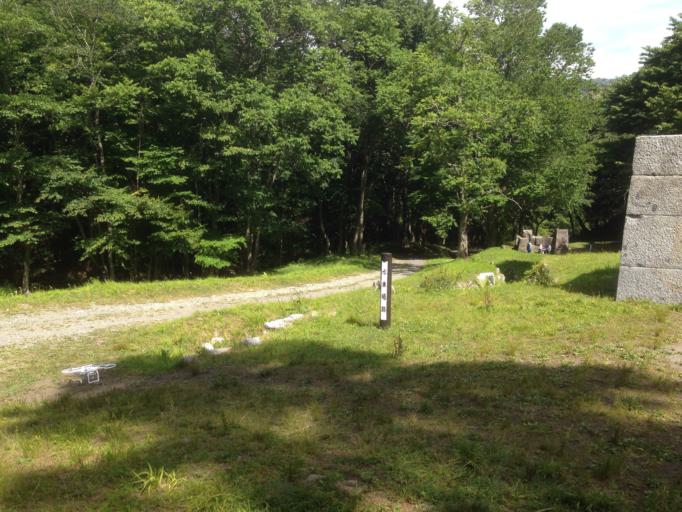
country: JP
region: Iwate
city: Tono
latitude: 39.3423
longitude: 141.6828
